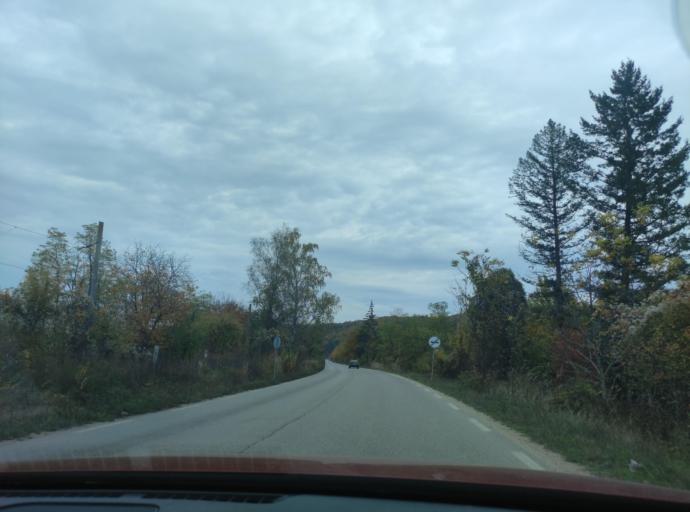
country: BG
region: Montana
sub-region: Obshtina Berkovitsa
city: Berkovitsa
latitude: 43.2546
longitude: 23.1713
